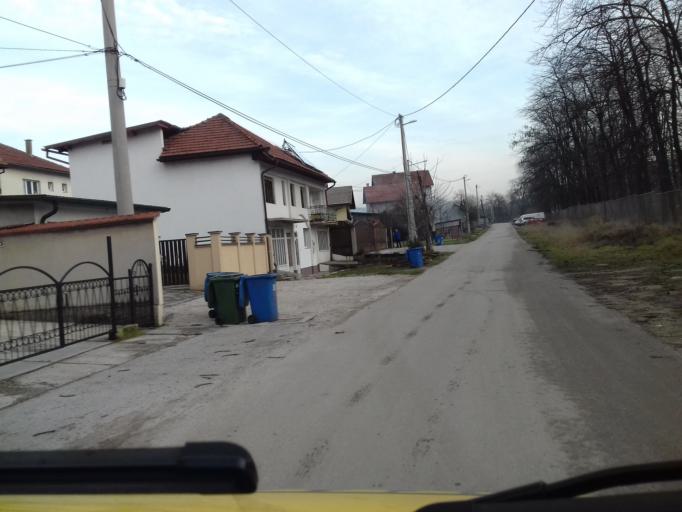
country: BA
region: Federation of Bosnia and Herzegovina
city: Zenica
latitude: 44.1945
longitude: 17.9243
